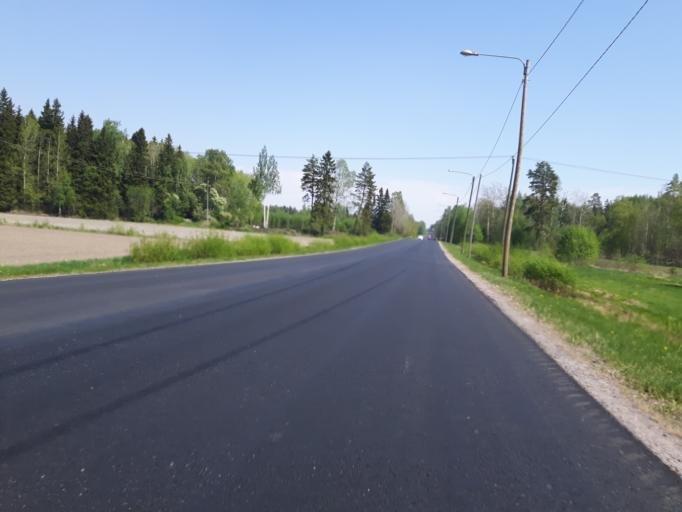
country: FI
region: Uusimaa
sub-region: Helsinki
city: Nickby
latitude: 60.3180
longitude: 25.4070
